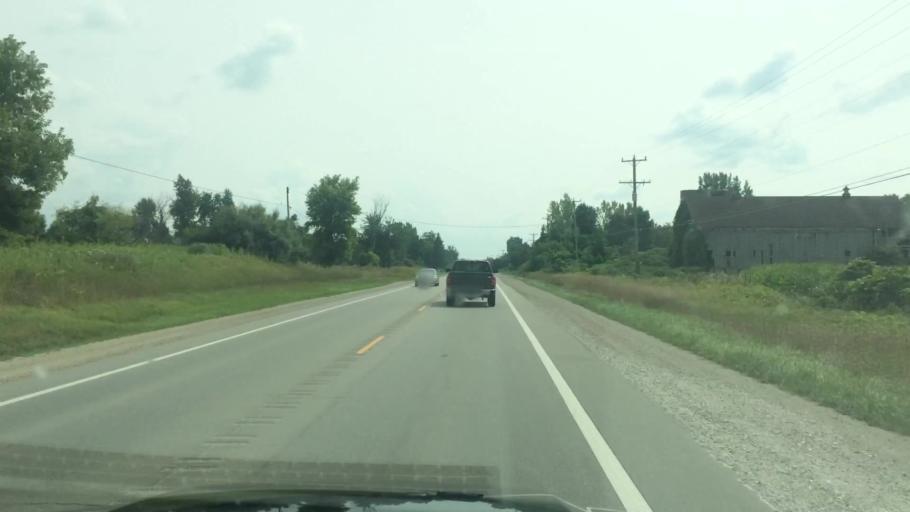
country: US
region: Michigan
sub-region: Oakland County
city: Oxford
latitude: 42.9214
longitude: -83.3129
